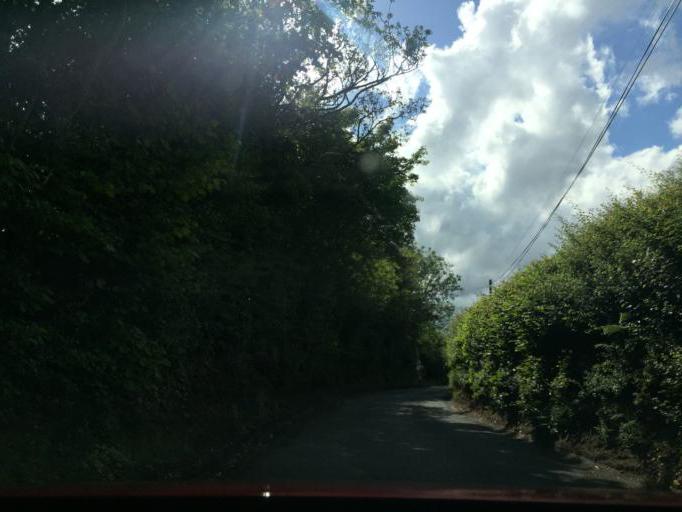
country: GB
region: England
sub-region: Hertfordshire
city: Wheathampstead
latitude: 51.8513
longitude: -0.3117
